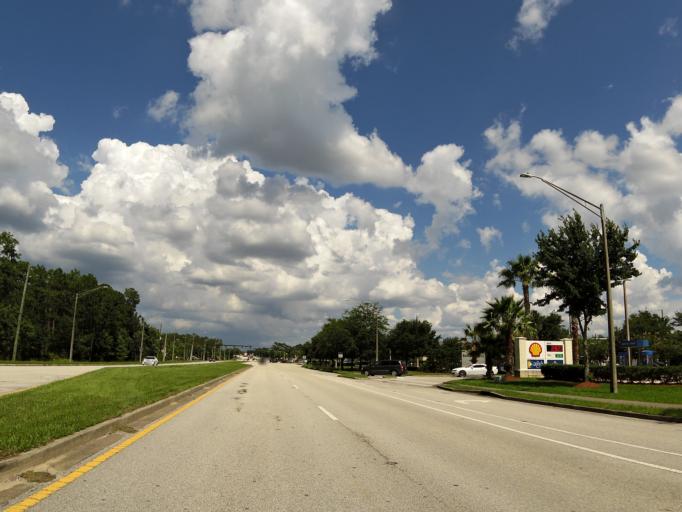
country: US
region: Florida
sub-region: Saint Johns County
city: Fruit Cove
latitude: 30.1424
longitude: -81.5495
